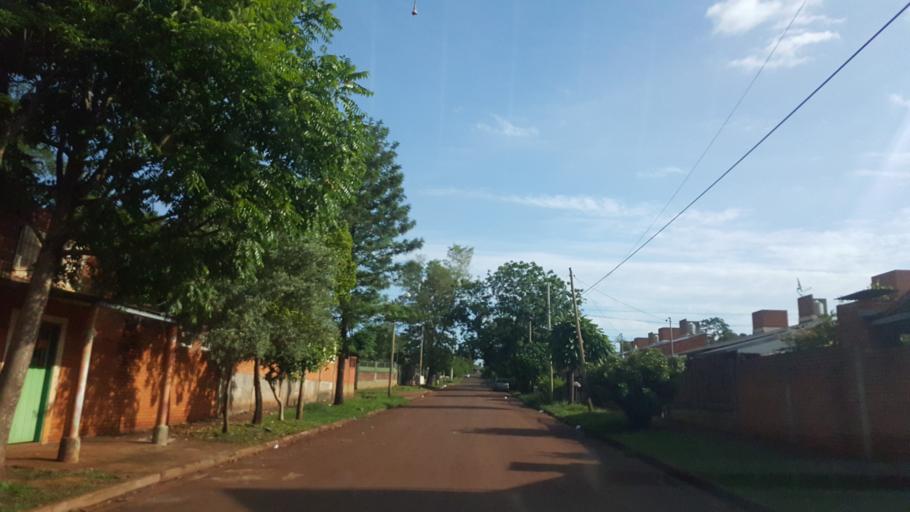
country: AR
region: Misiones
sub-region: Departamento de Capital
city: Posadas
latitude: -27.4230
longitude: -55.9236
